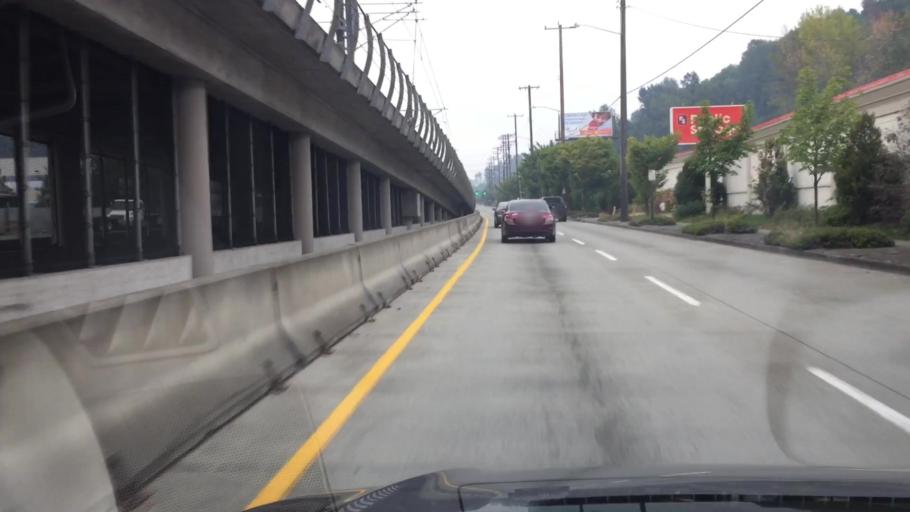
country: US
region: Washington
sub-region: King County
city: Riverton
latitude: 47.5100
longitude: -122.2783
